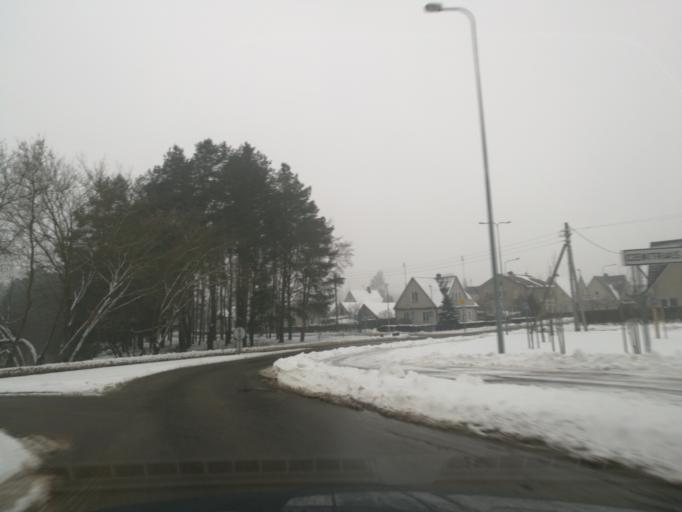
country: LT
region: Utenos apskritis
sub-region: Anyksciai
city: Anyksciai
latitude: 55.5158
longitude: 25.0923
